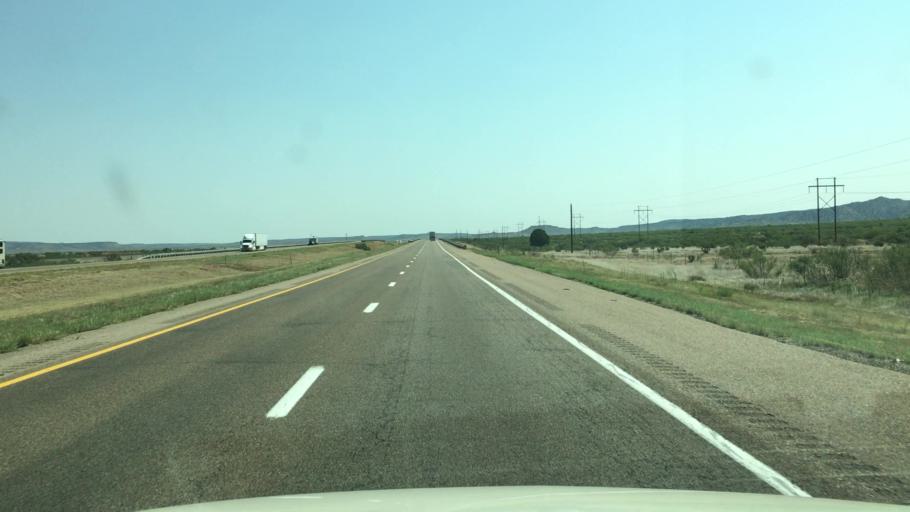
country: US
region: New Mexico
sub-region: Quay County
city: Tucumcari
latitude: 35.1106
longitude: -104.0082
